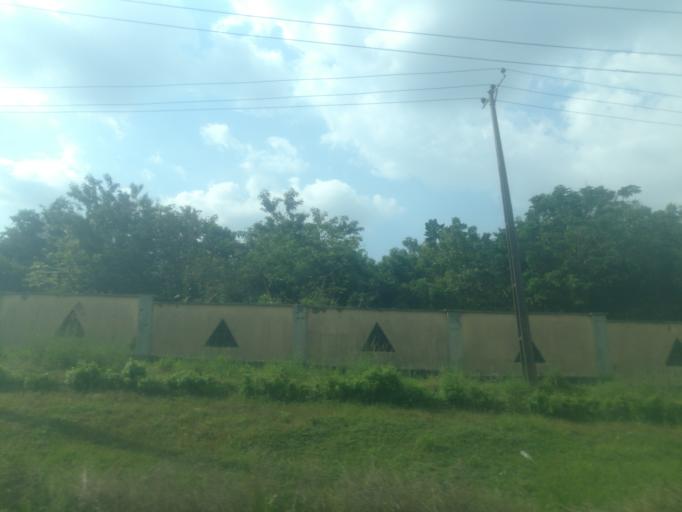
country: NG
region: Ogun
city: Abeokuta
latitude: 7.1325
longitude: 3.3040
